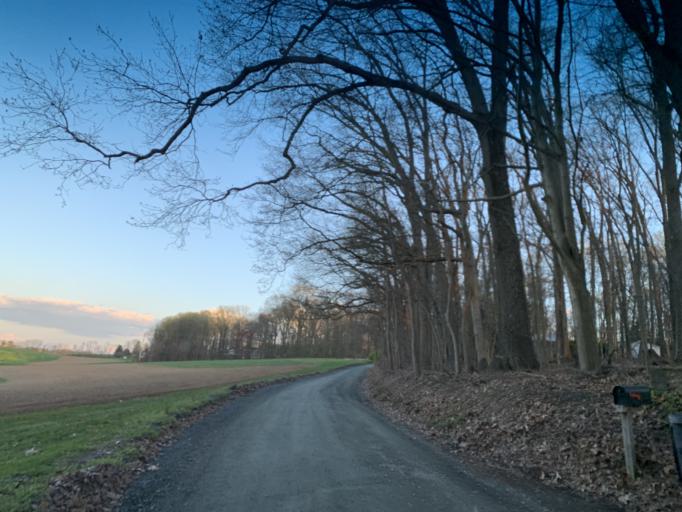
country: US
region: Maryland
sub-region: Harford County
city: Bel Air North
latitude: 39.6168
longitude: -76.3599
